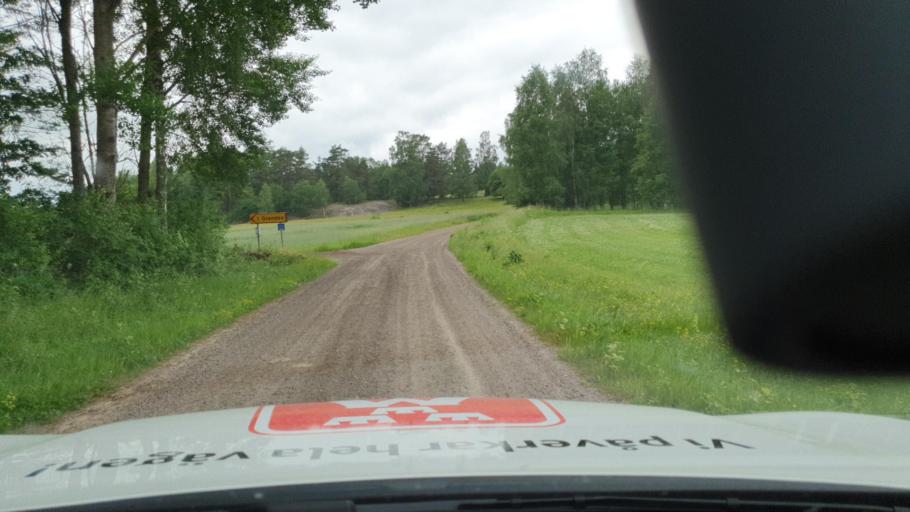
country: SE
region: Vaestra Goetaland
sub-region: Hjo Kommun
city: Hjo
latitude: 58.3450
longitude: 14.3105
